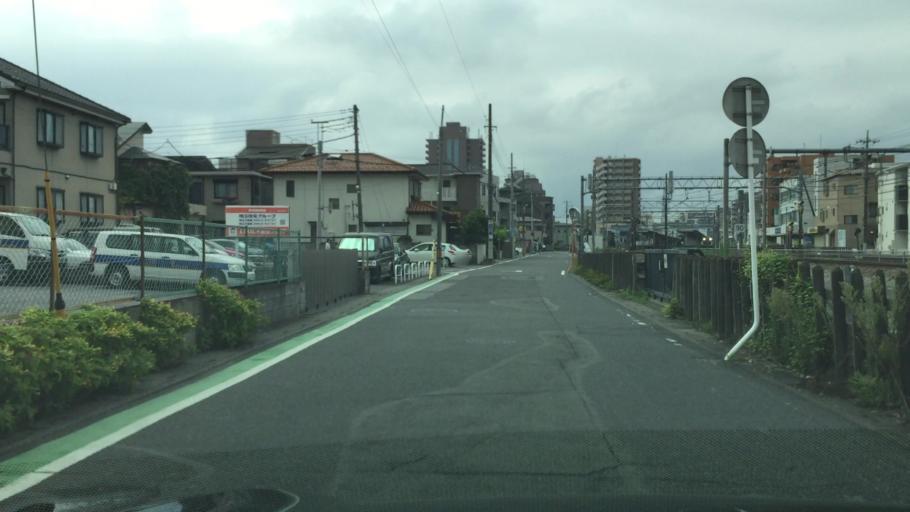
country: JP
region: Saitama
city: Ageoshimo
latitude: 35.9445
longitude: 139.6084
